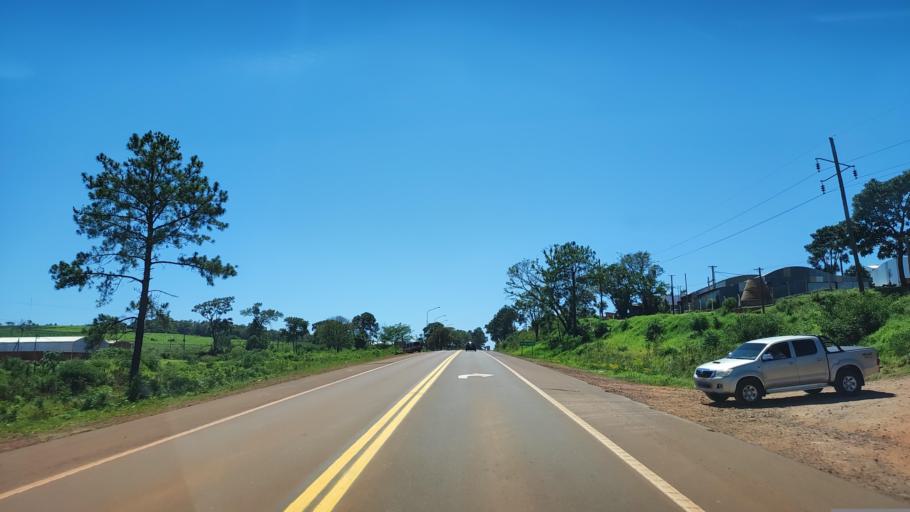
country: AR
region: Misiones
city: Aristobulo del Valle
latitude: -27.0838
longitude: -54.8189
